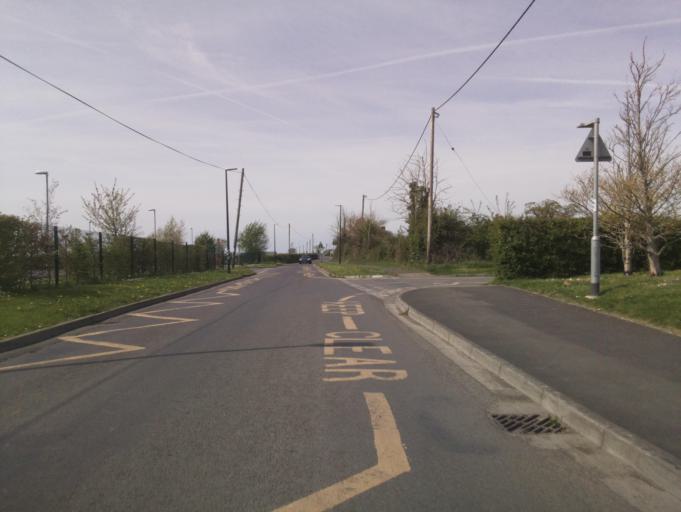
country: GB
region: England
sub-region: Somerset
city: Yeovil
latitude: 51.0177
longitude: -2.5796
